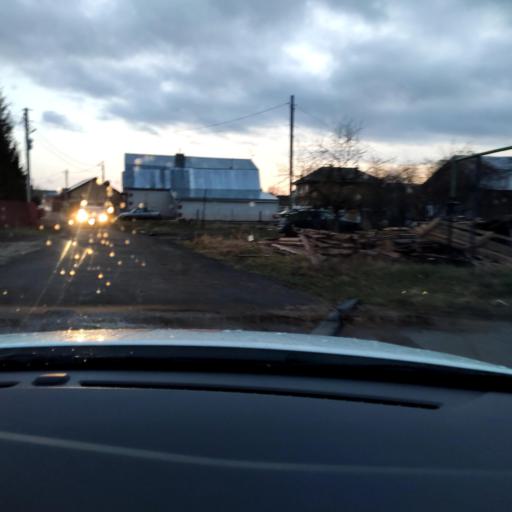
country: RU
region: Tatarstan
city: Stolbishchi
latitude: 55.6952
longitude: 49.1574
